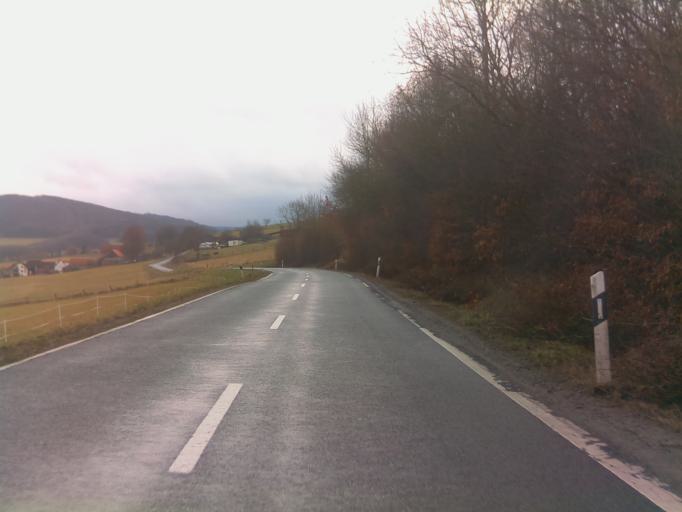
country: DE
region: Hesse
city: Tann
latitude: 50.6284
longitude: 10.0201
